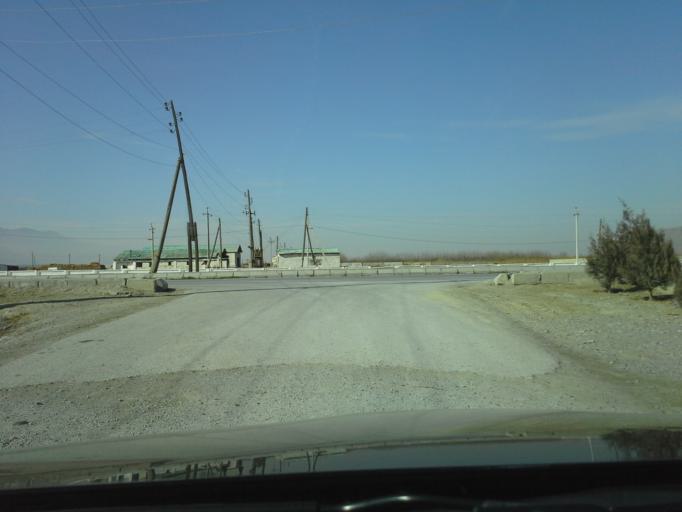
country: TM
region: Ahal
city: Abadan
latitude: 38.1056
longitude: 58.0296
